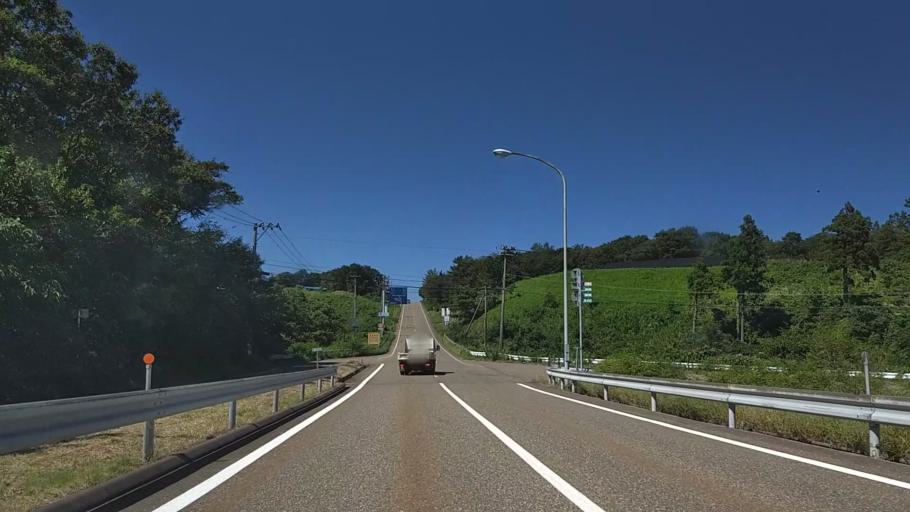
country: JP
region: Niigata
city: Joetsu
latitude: 37.1691
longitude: 138.1098
